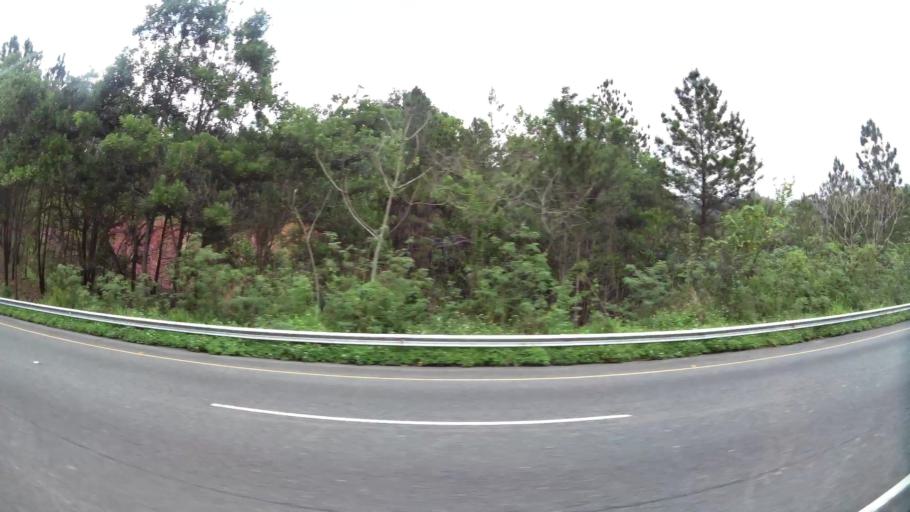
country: DO
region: Monsenor Nouel
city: Piedra Blanca
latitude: 18.8003
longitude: -70.2767
